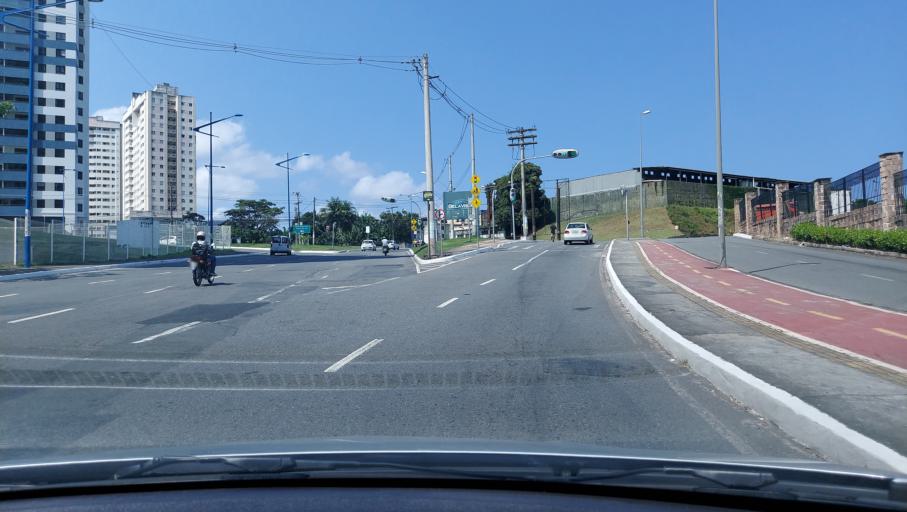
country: BR
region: Bahia
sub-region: Salvador
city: Salvador
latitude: -12.9663
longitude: -38.4741
